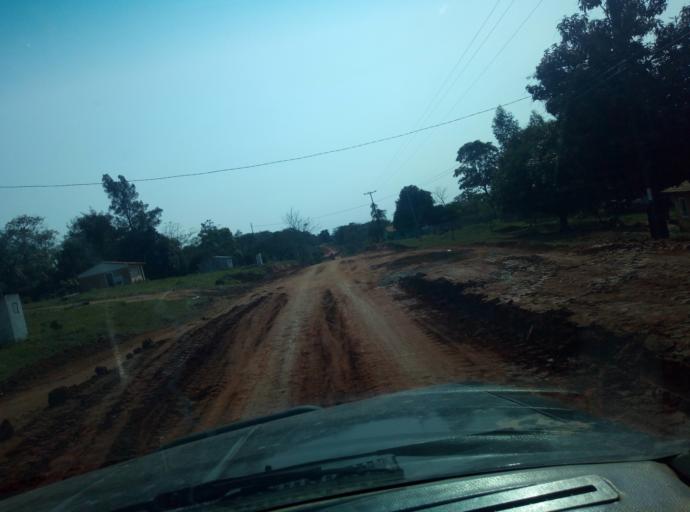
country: PY
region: Caaguazu
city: Carayao
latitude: -25.3112
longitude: -56.3261
